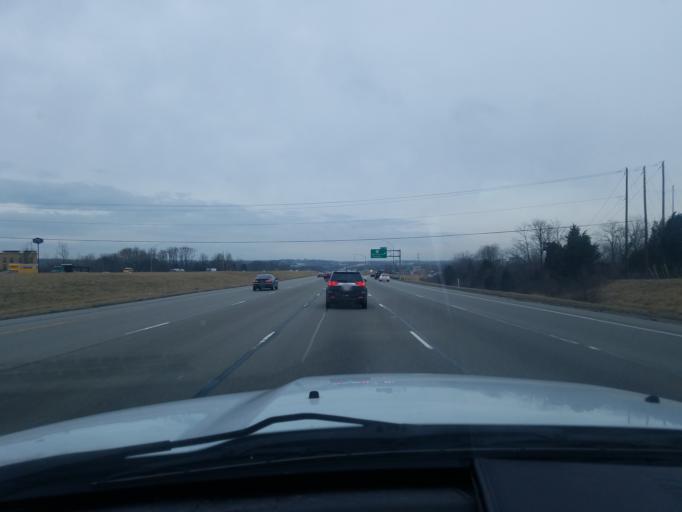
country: US
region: Ohio
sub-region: Warren County
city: Springboro
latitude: 39.5671
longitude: -84.2651
